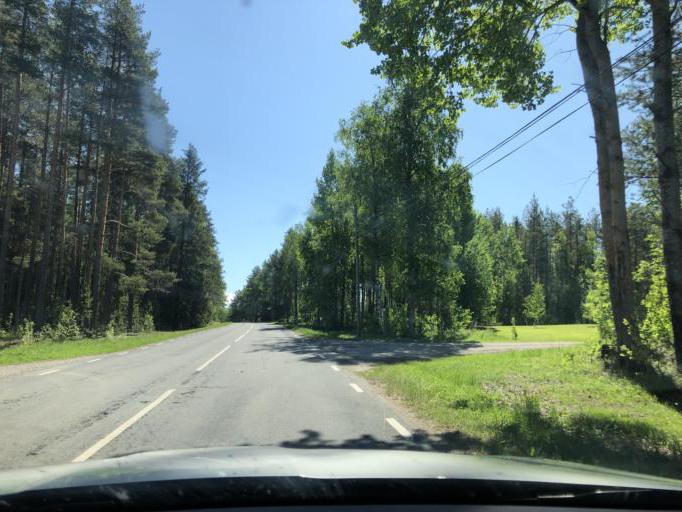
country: SE
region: Norrbotten
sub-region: Lulea Kommun
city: Sodra Sunderbyn
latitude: 65.6619
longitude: 21.9761
